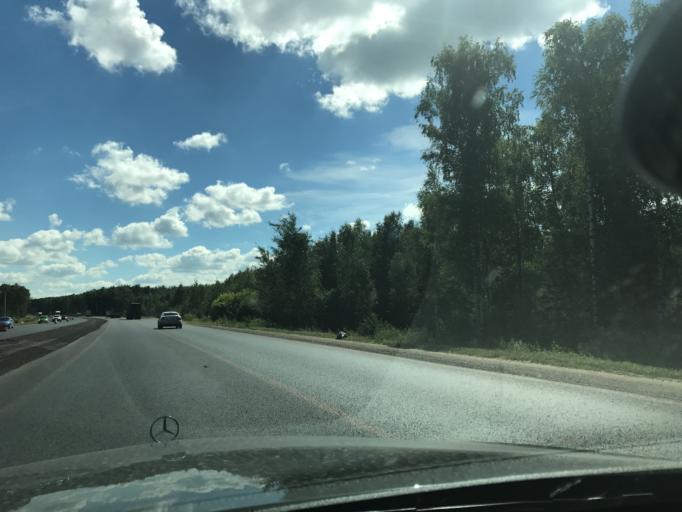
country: RU
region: Nizjnij Novgorod
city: Gorbatovka
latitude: 56.2530
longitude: 43.7116
